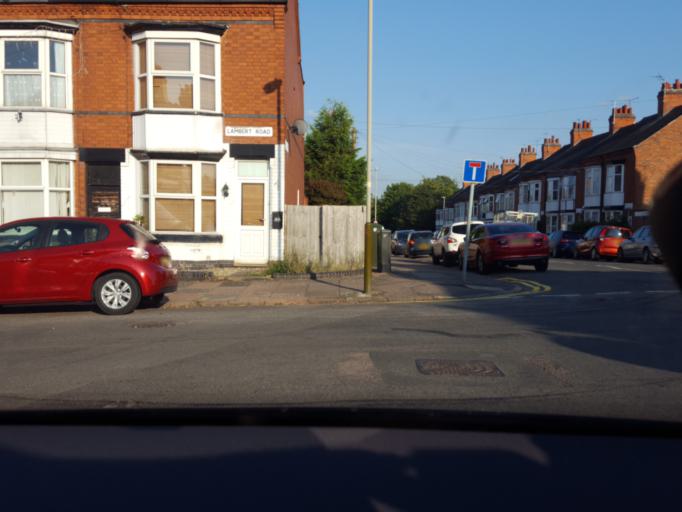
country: GB
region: England
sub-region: City of Leicester
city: Leicester
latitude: 52.6202
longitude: -1.1525
